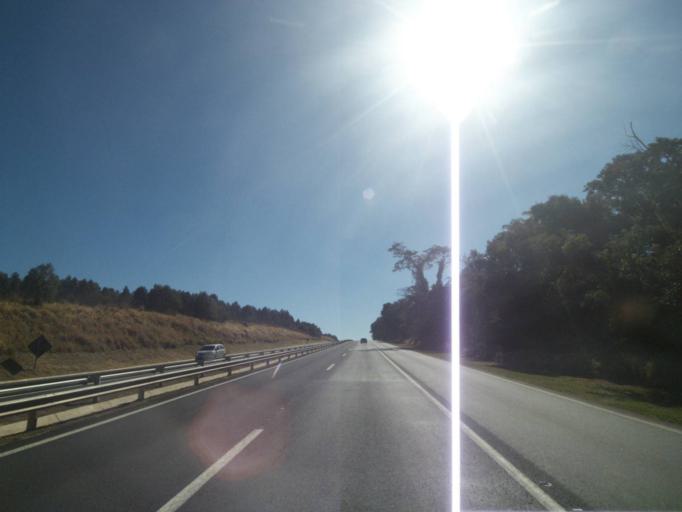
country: BR
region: Parana
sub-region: Tibagi
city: Tibagi
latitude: -24.8472
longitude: -50.4738
